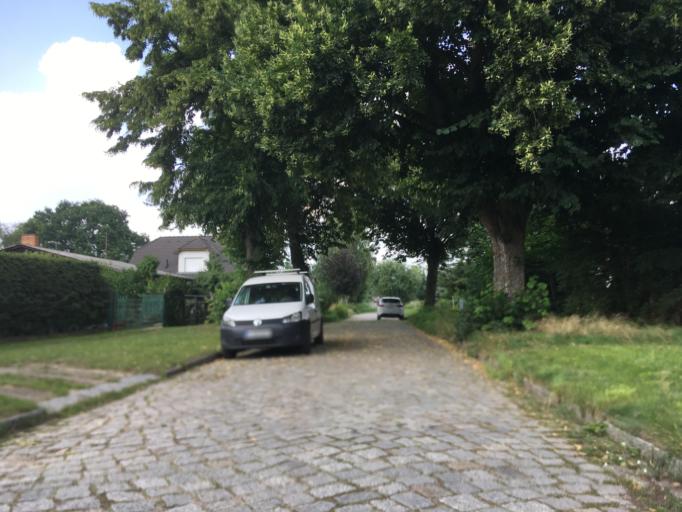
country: DE
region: Brandenburg
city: Bernau bei Berlin
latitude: 52.6520
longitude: 13.5481
